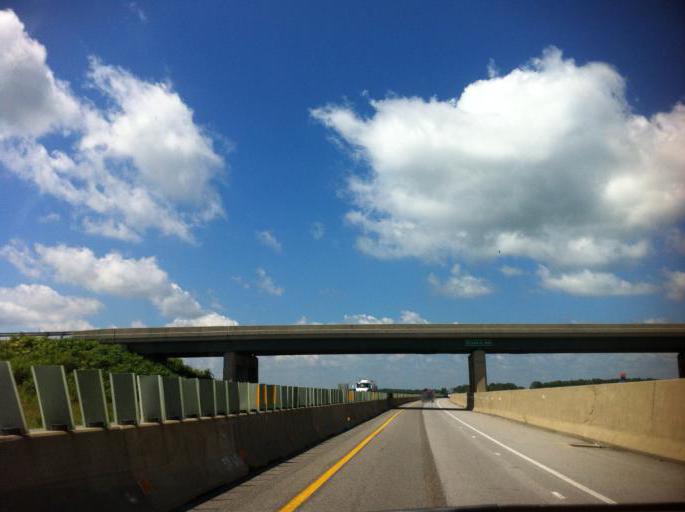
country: US
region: Ohio
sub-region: Sandusky County
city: Clyde
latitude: 41.3622
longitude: -82.9349
